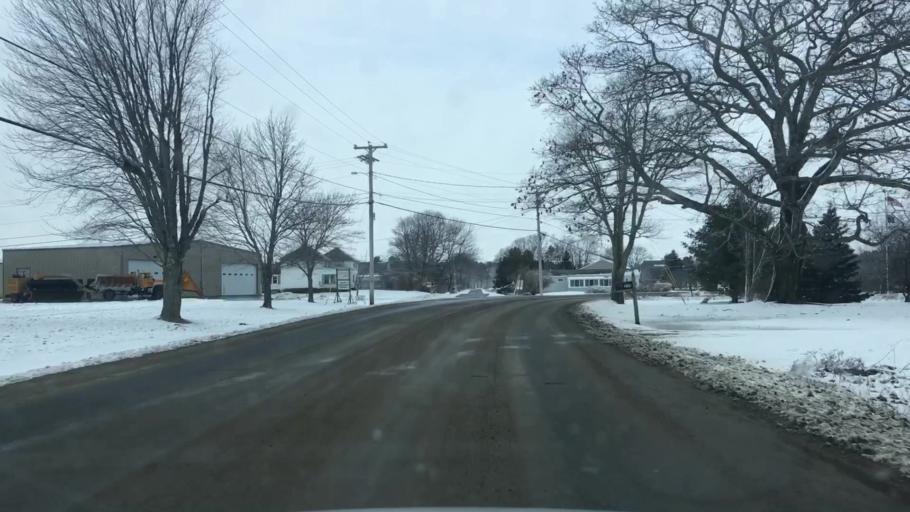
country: US
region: Maine
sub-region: Knox County
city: South Thomaston
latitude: 44.0622
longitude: -69.0923
